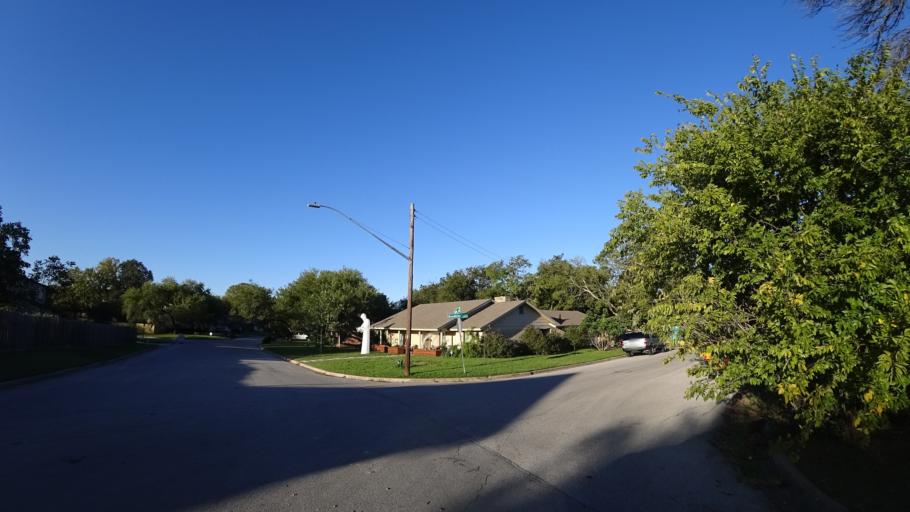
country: US
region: Texas
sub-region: Travis County
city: Austin
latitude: 30.3000
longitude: -97.6757
